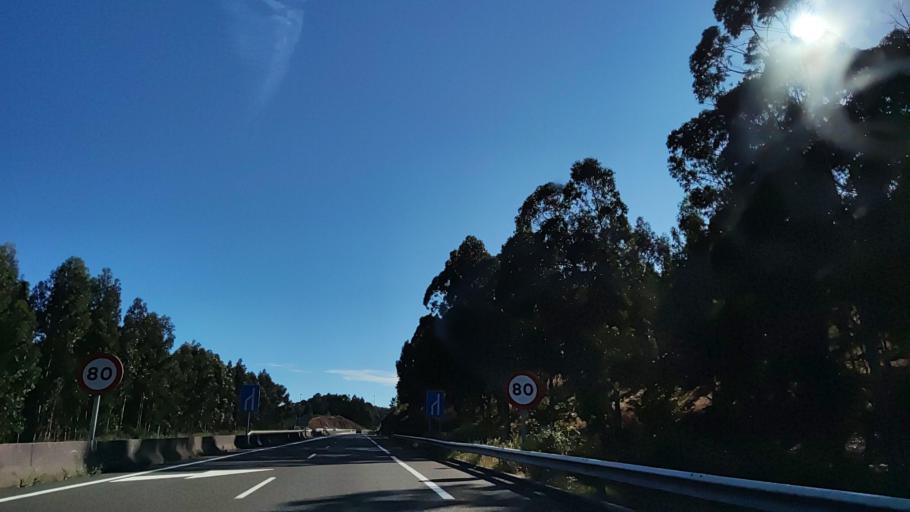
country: ES
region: Galicia
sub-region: Provincia da Coruna
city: Boiro
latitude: 42.5769
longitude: -8.9905
